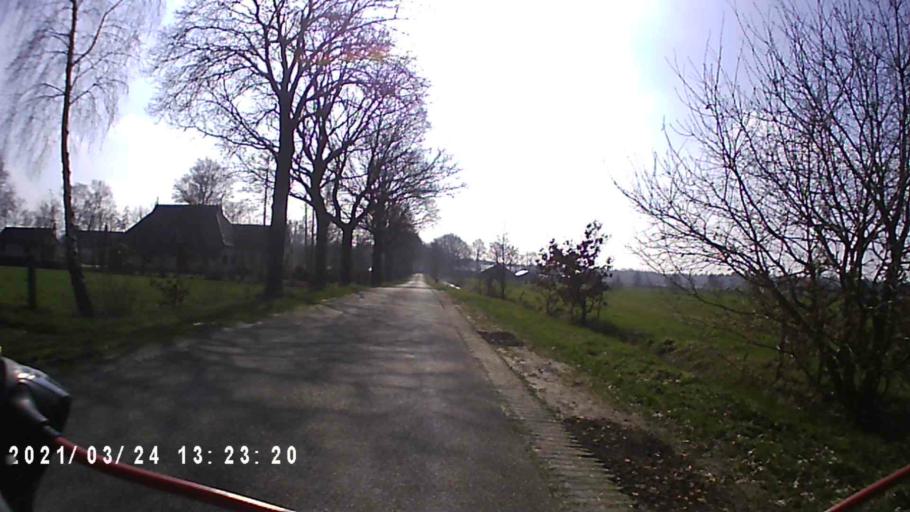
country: NL
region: Groningen
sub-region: Gemeente Grootegast
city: Grootegast
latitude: 53.0994
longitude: 6.2760
